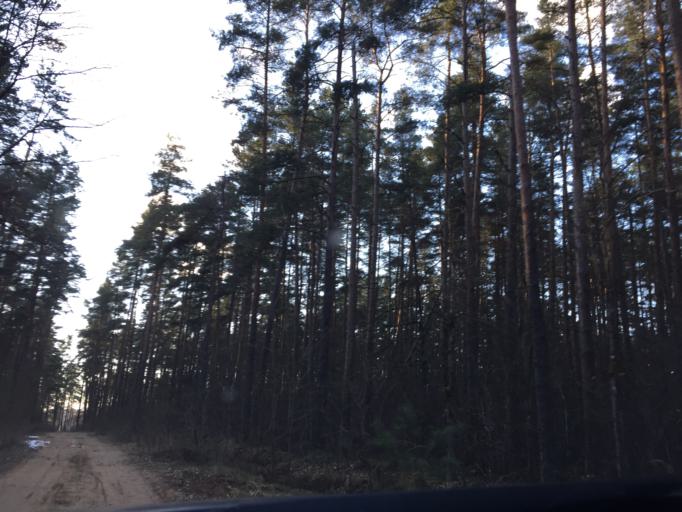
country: LV
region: Kekava
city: Kekava
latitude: 56.8656
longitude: 24.2030
